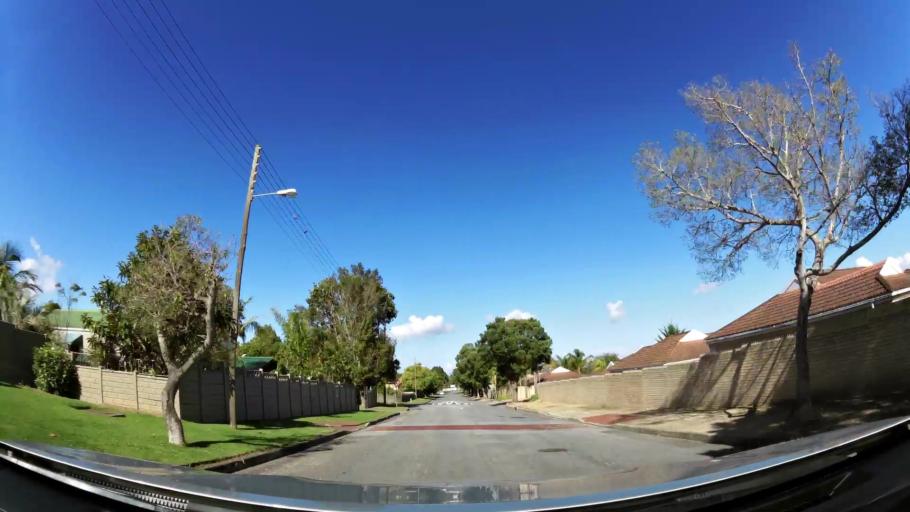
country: ZA
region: Western Cape
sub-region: Eden District Municipality
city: George
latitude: -33.9409
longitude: 22.4718
